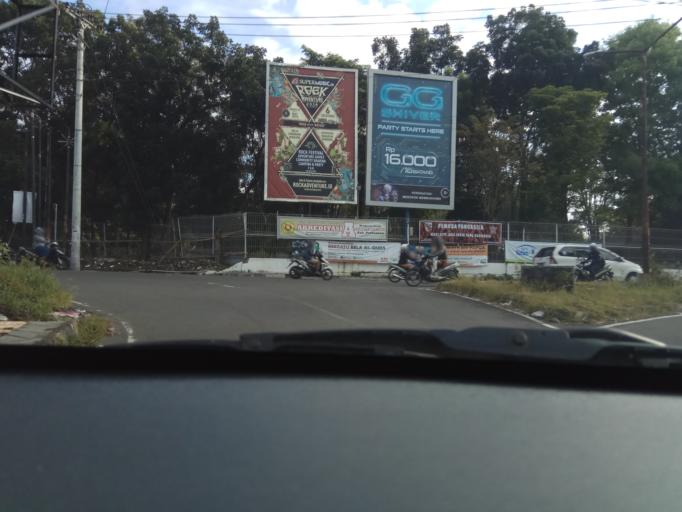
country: ID
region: Daerah Istimewa Yogyakarta
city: Depok
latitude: -7.7644
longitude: 110.4110
